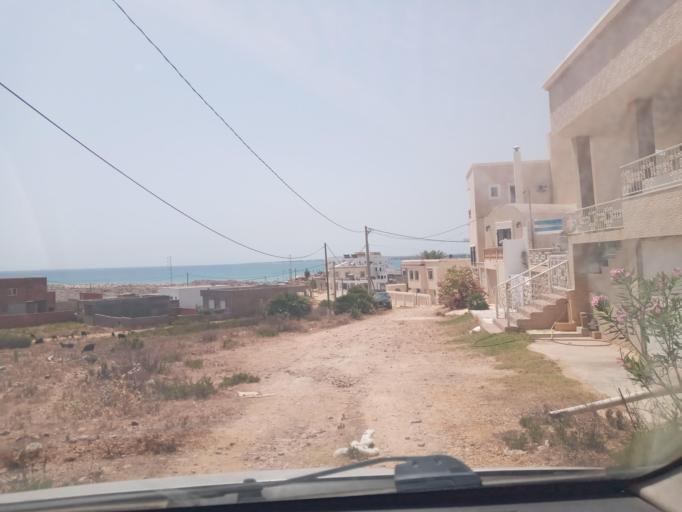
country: TN
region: Nabul
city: El Haouaria
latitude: 37.0432
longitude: 11.0615
